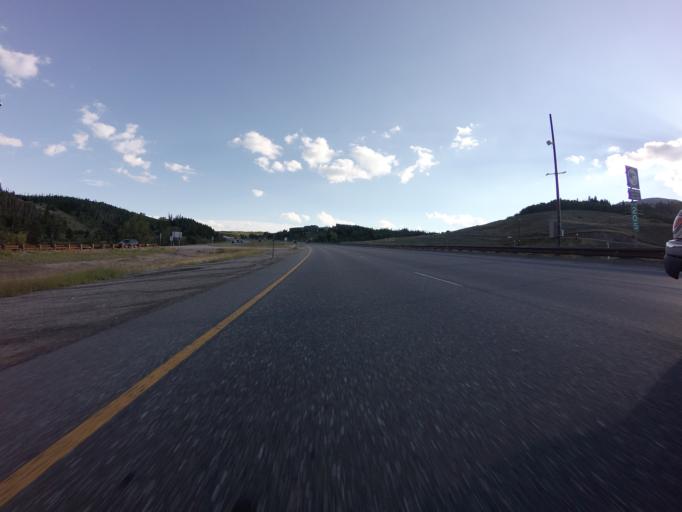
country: US
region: Colorado
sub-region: Summit County
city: Silverthorne
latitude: 39.6245
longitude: -106.0728
